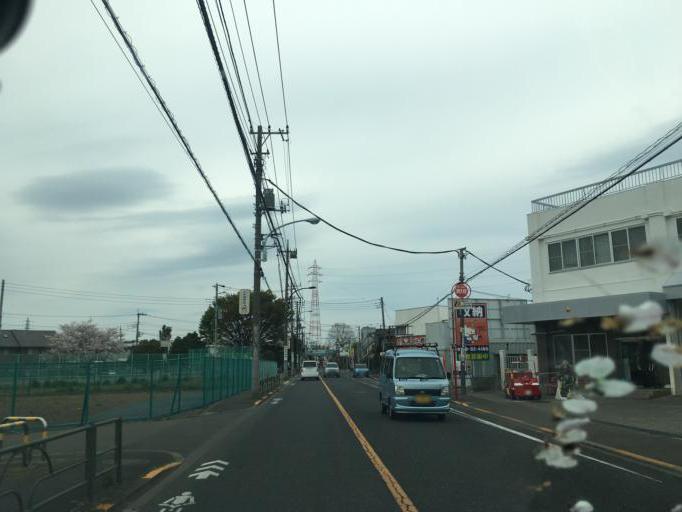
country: JP
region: Tokyo
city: Mitaka-shi
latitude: 35.6736
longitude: 139.5547
